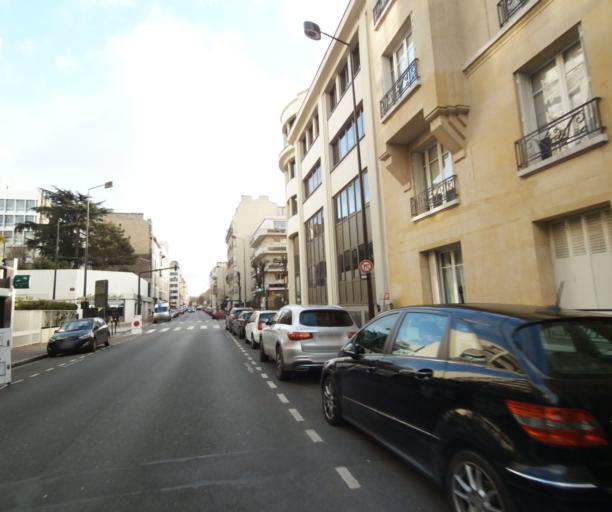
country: FR
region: Ile-de-France
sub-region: Departement des Hauts-de-Seine
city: Levallois-Perret
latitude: 48.8886
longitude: 2.2812
